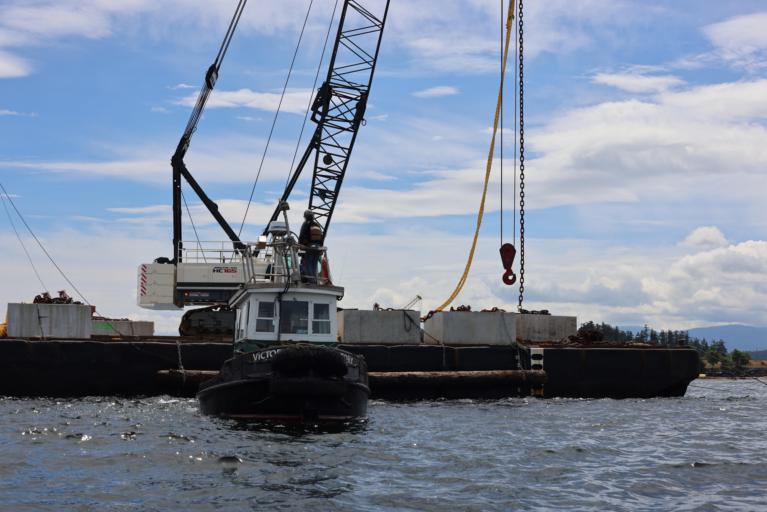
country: CA
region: British Columbia
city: Nanaimo
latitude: 49.1562
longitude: -123.8849
